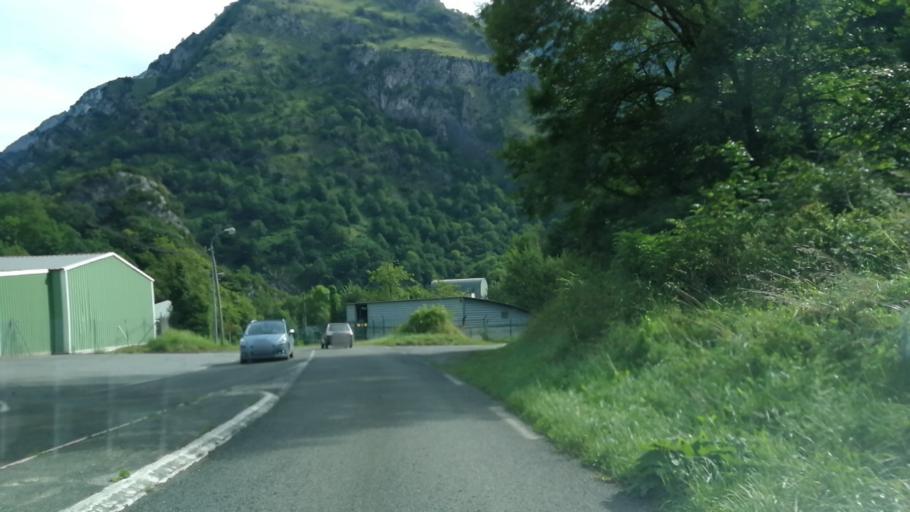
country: FR
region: Aquitaine
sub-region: Departement des Pyrenees-Atlantiques
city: Arette
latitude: 42.9420
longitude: -0.6141
